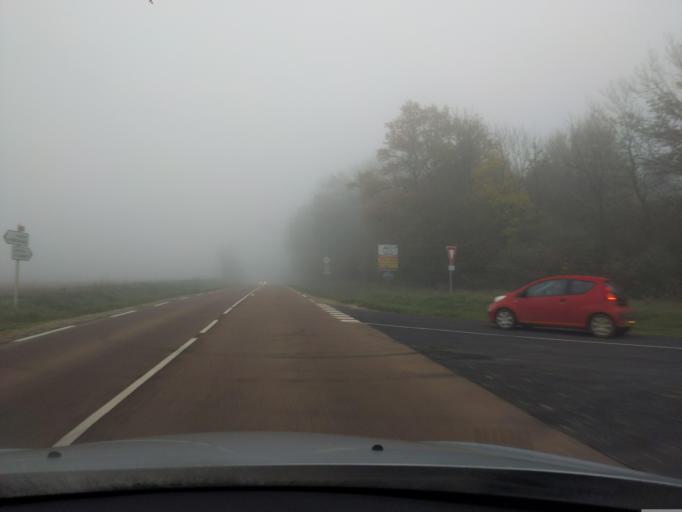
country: FR
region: Champagne-Ardenne
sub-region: Departement de la Haute-Marne
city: Langres
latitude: 47.8167
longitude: 5.2951
